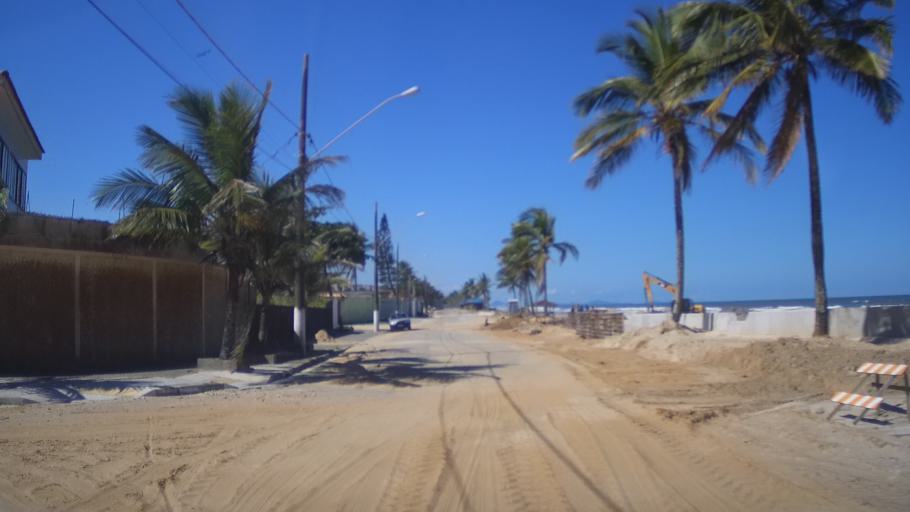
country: BR
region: Sao Paulo
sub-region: Mongagua
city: Mongagua
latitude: -24.1265
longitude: -46.6798
